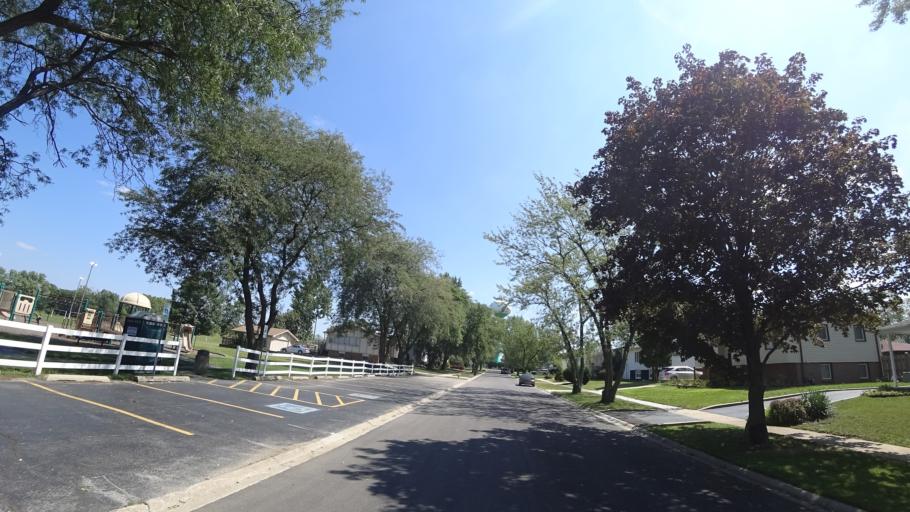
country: US
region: Illinois
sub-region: Cook County
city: Orland Park
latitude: 41.6253
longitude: -87.8368
